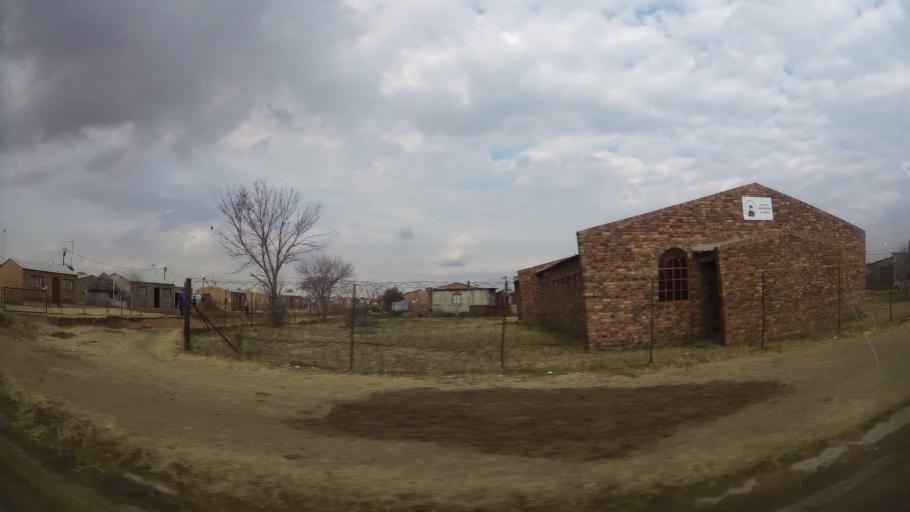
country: ZA
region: Orange Free State
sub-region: Fezile Dabi District Municipality
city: Sasolburg
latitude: -26.8404
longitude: 27.8573
